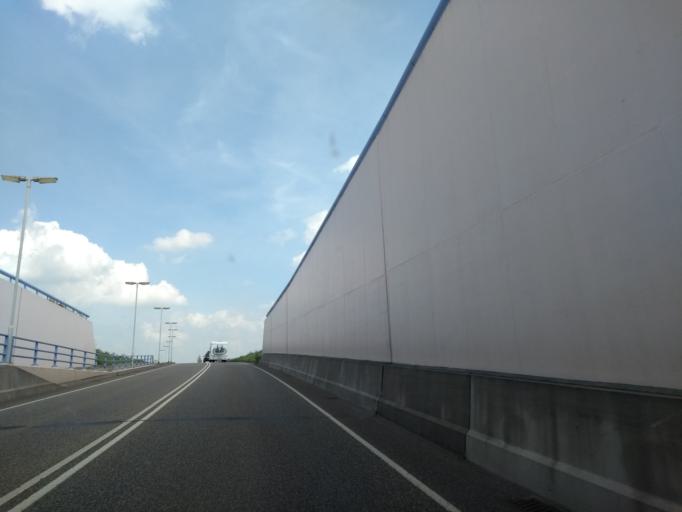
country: NL
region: Friesland
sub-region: Sudwest Fryslan
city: Oppenhuizen
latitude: 53.0268
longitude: 5.6837
